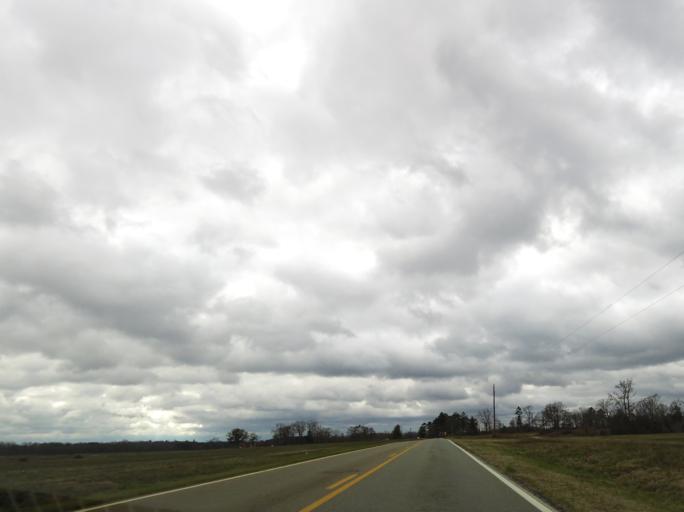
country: US
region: Georgia
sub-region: Twiggs County
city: Jeffersonville
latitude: 32.5419
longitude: -83.3732
